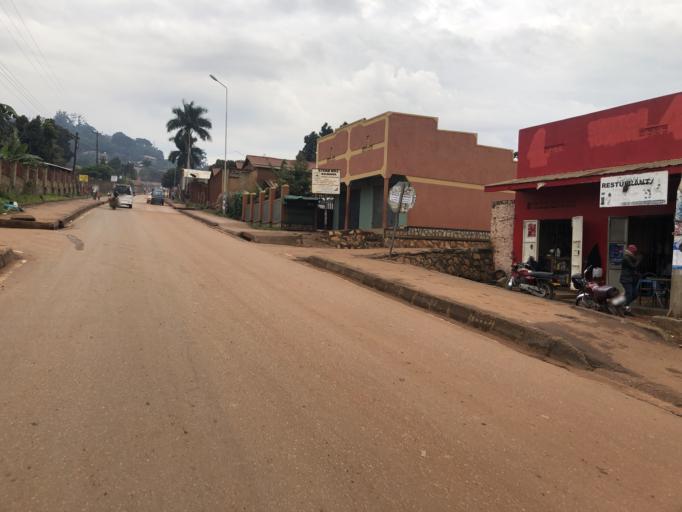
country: UG
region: Central Region
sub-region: Kampala District
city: Kampala
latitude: 0.2808
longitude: 32.6014
